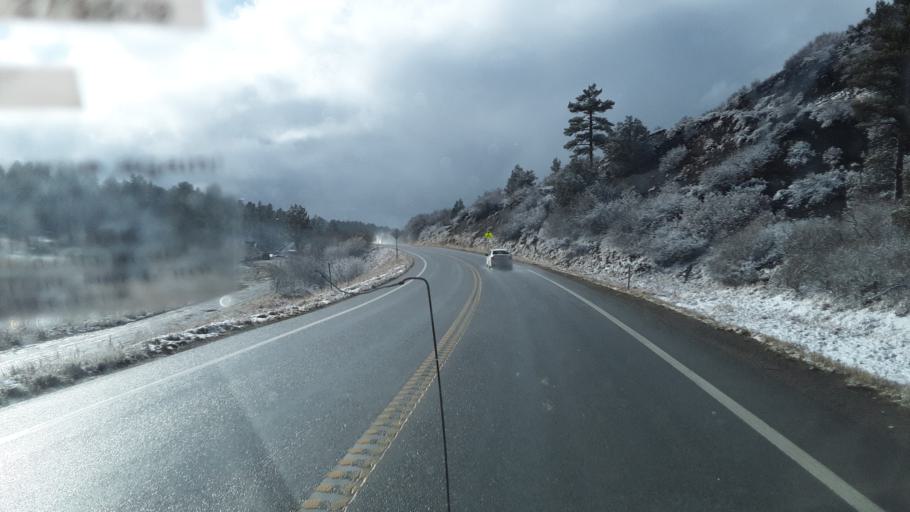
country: US
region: Colorado
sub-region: Archuleta County
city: Pagosa Springs
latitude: 37.2390
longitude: -107.1584
